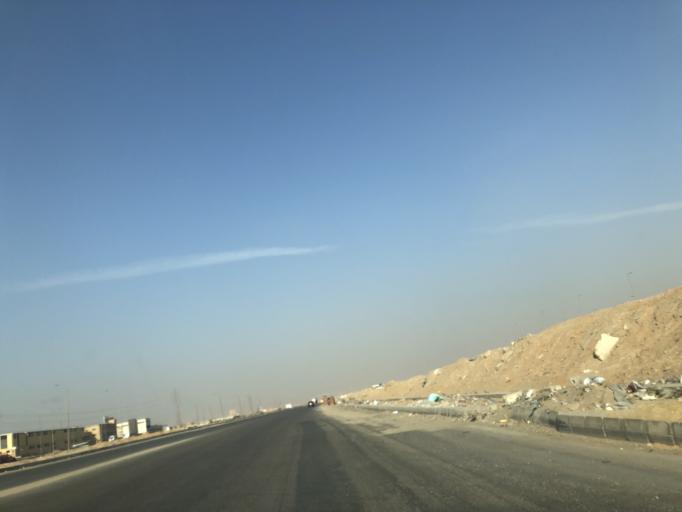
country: EG
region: Al Jizah
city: Madinat Sittah Uktubar
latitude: 29.8953
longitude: 30.8982
